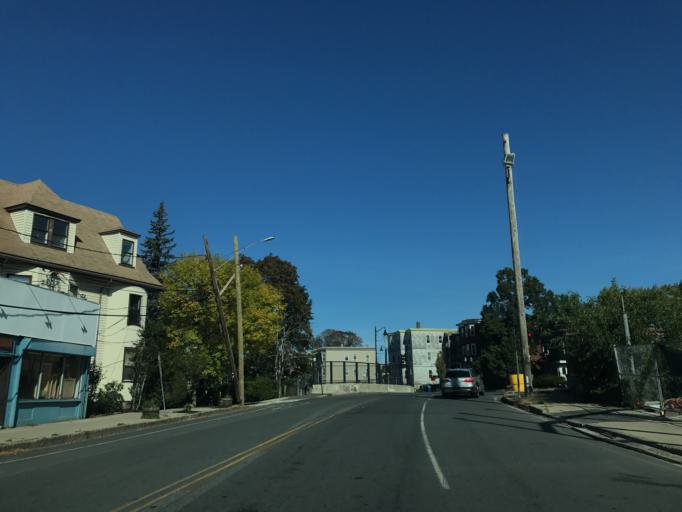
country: US
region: Massachusetts
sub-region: Middlesex County
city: Cambridge
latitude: 42.3863
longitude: -71.1161
